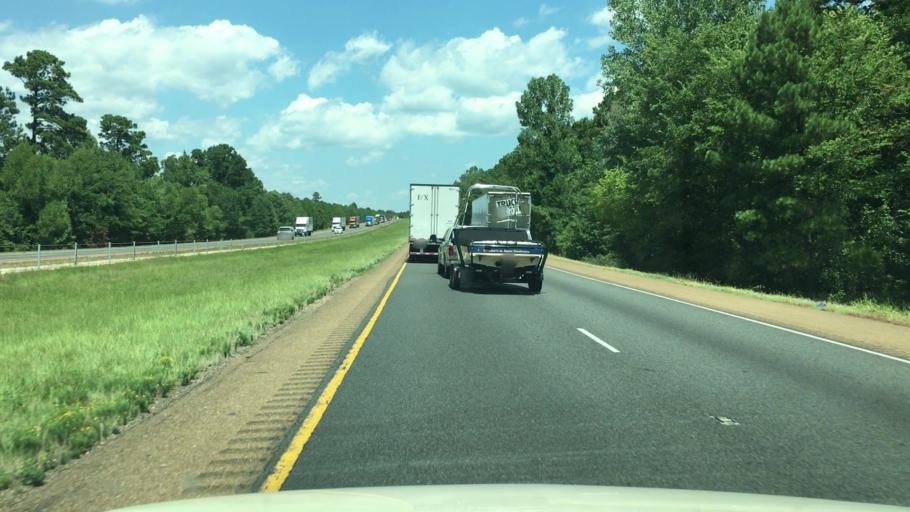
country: US
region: Arkansas
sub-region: Clark County
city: Gurdon
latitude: 33.9455
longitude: -93.2395
